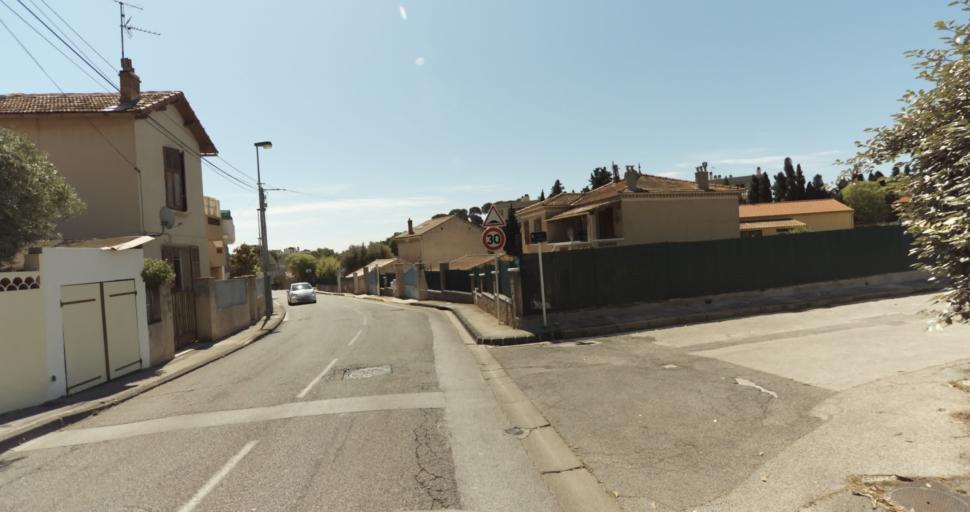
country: FR
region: Provence-Alpes-Cote d'Azur
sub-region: Departement du Var
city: Le Revest-les-Eaux
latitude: 43.1454
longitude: 5.9040
